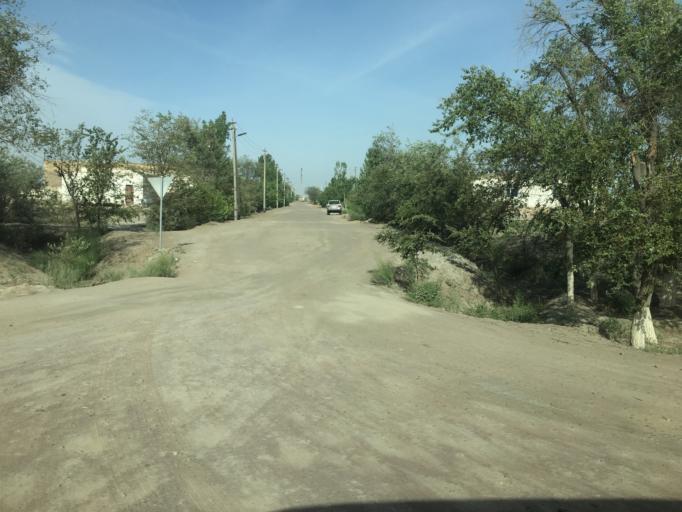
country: TM
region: Dasoguz
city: Dasoguz
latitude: 41.7838
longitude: 59.9538
